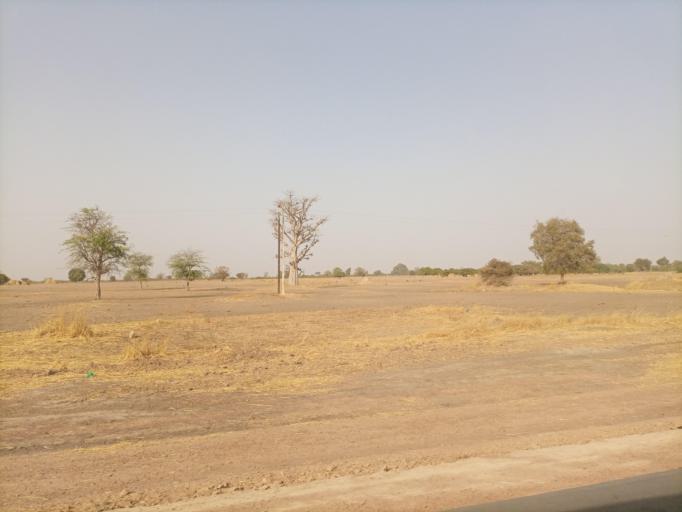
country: SN
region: Fatick
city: Passi
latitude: 14.0257
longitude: -16.3033
